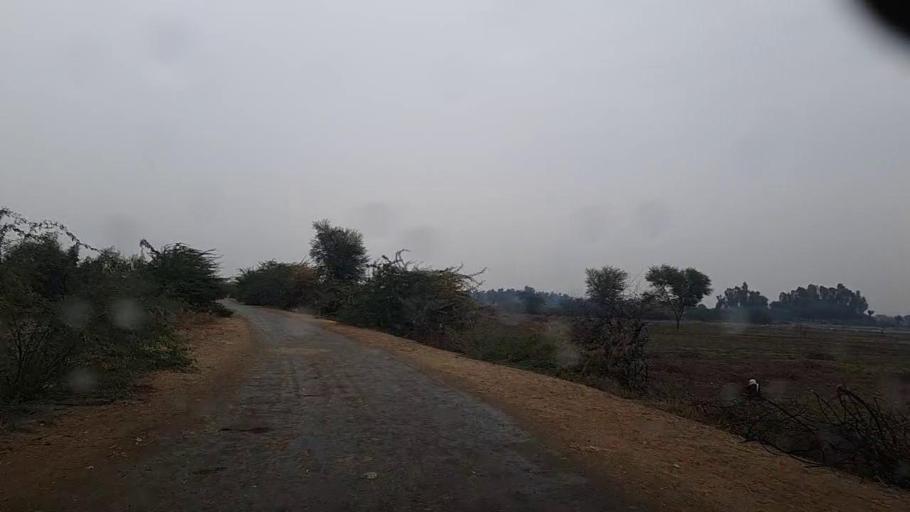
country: PK
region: Sindh
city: Ranipur
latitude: 27.2587
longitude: 68.5753
